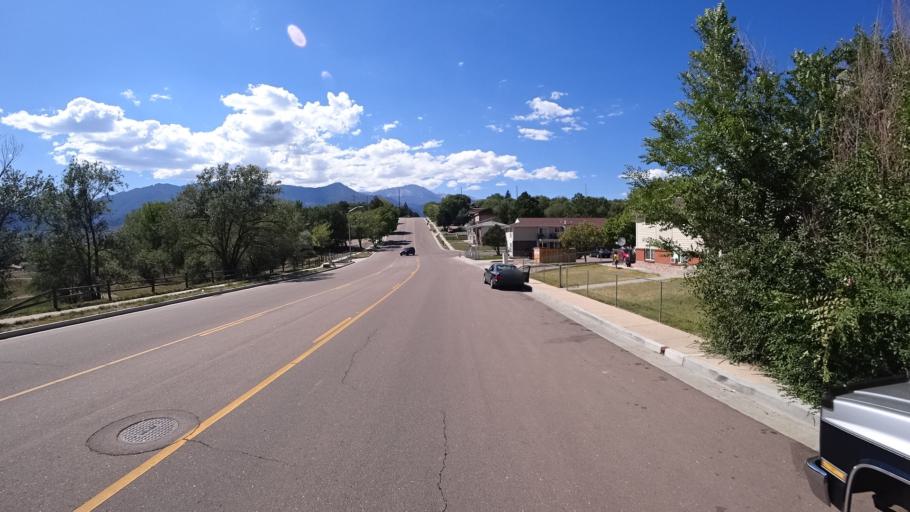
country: US
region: Colorado
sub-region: El Paso County
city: Colorado Springs
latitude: 38.8558
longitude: -104.8557
